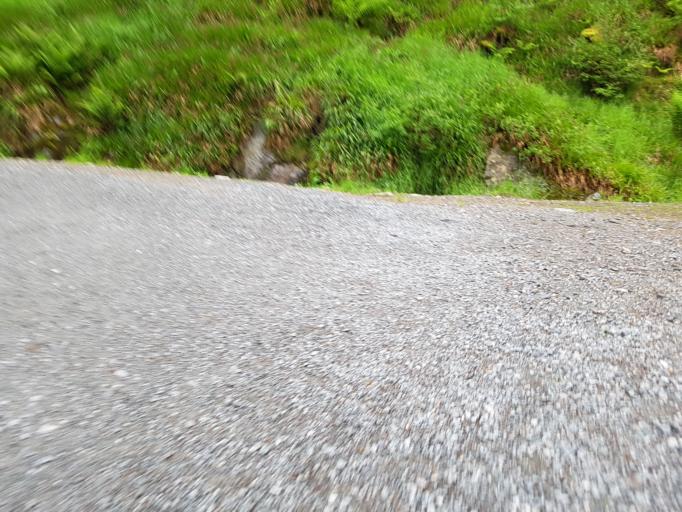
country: NO
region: Hordaland
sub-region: Bergen
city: Bergen
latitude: 60.3959
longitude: 5.3401
